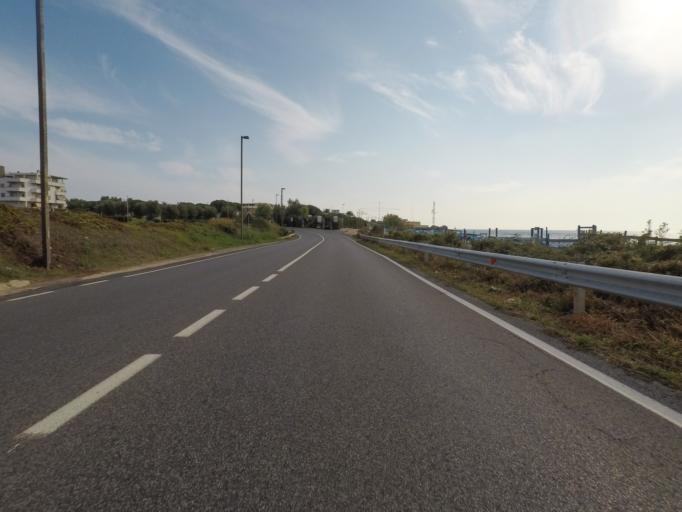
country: IT
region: Latium
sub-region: Citta metropolitana di Roma Capitale
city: Santa Marinella
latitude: 42.0364
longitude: 11.8331
